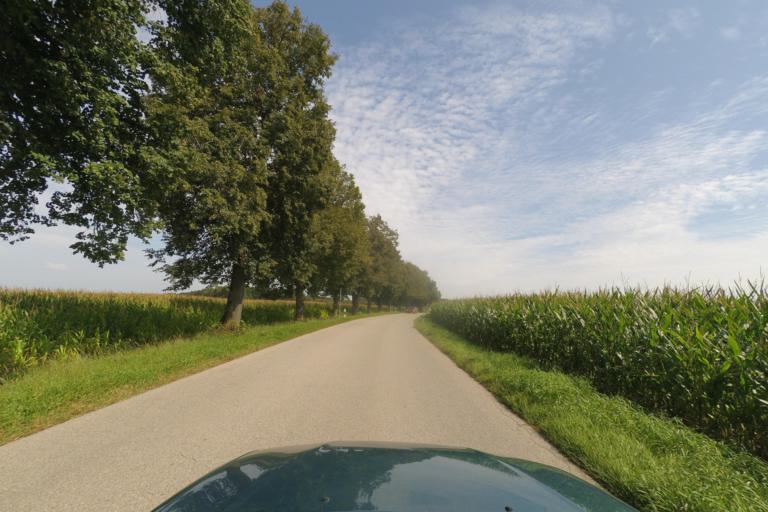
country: DE
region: Bavaria
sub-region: Upper Bavaria
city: Grasbrunn
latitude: 48.0609
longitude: 11.7780
